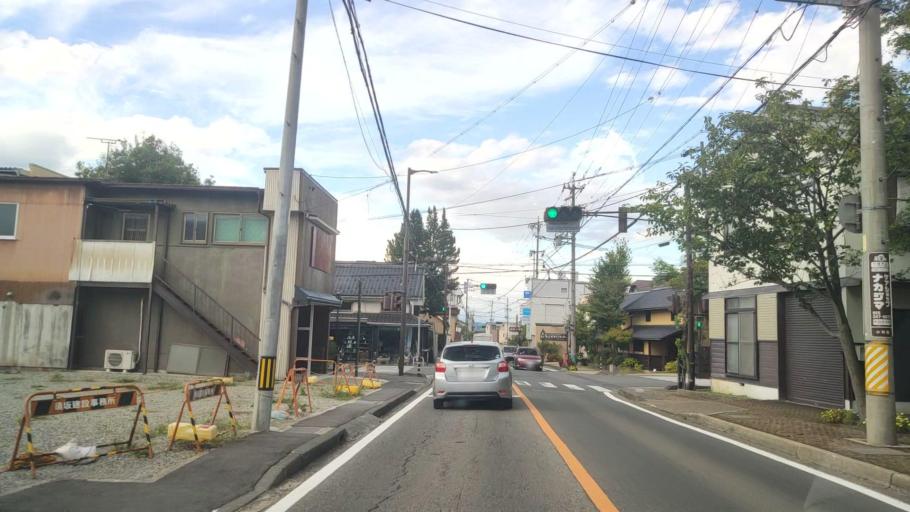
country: JP
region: Nagano
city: Suzaka
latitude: 36.6956
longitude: 138.3160
